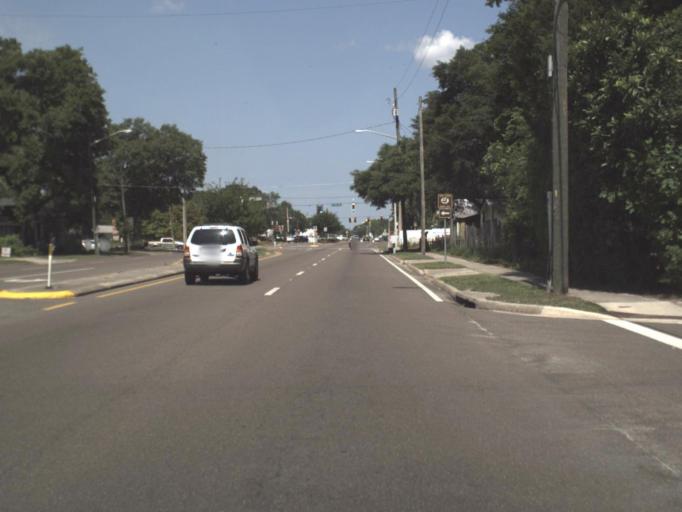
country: US
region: Florida
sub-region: Alachua County
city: Gainesville
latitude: 29.6520
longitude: -82.3044
